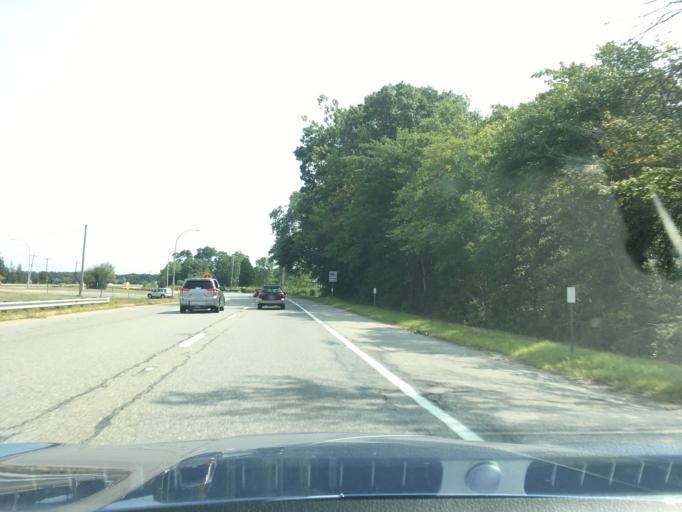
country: US
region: Rhode Island
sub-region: Bristol County
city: Barrington
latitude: 41.7684
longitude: -71.3233
